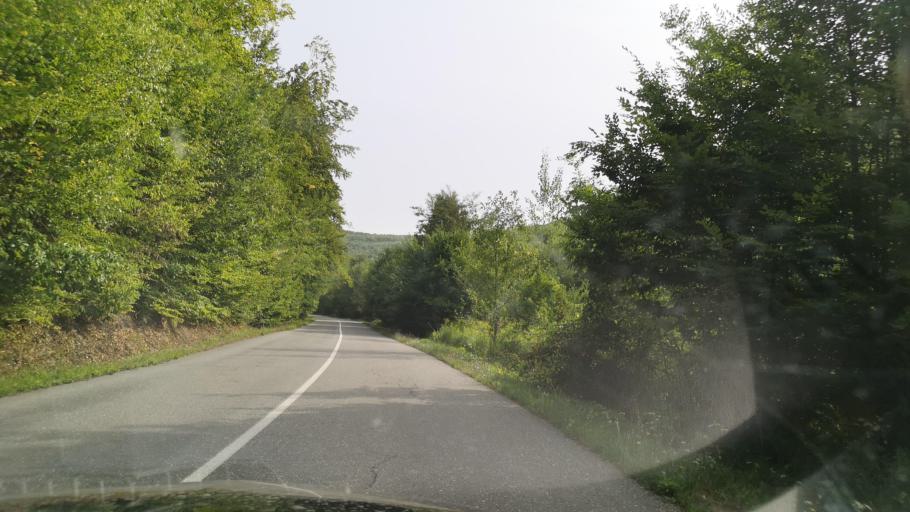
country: SK
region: Banskobystricky
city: Tisovec
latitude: 48.5767
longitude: 19.9712
